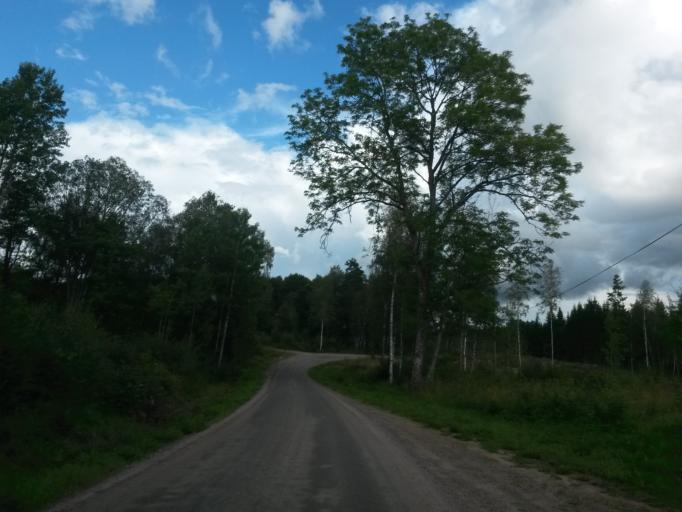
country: SE
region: Vaestra Goetaland
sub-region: Herrljunga Kommun
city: Herrljunga
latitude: 58.0393
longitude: 13.0400
